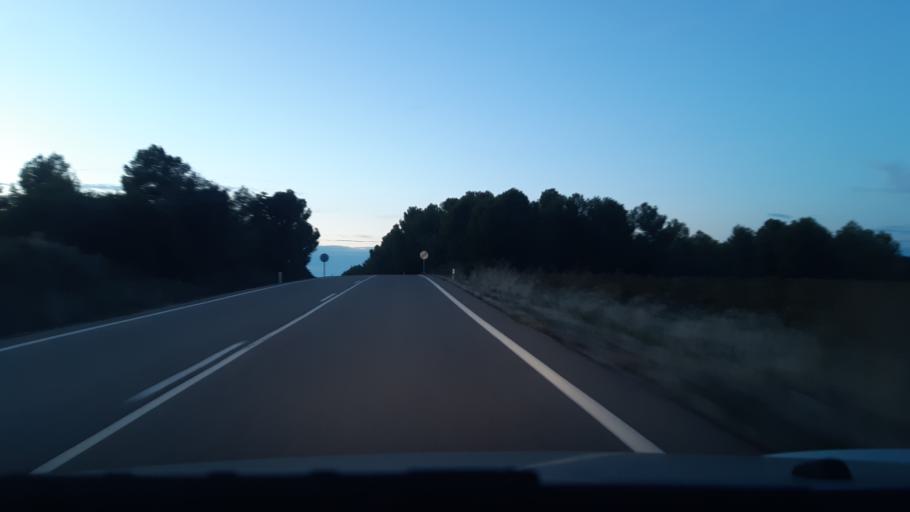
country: ES
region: Aragon
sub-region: Provincia de Teruel
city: Calaceite
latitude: 40.9616
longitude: 0.2126
